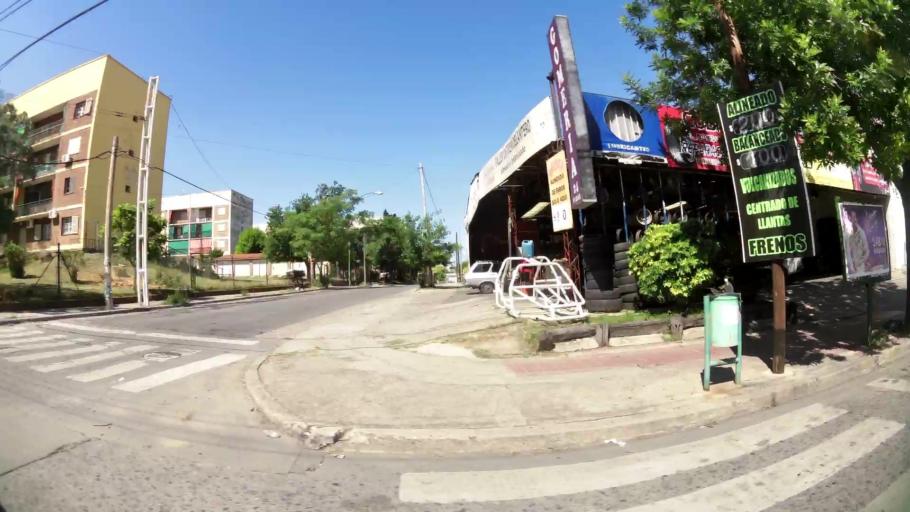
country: AR
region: Cordoba
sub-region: Departamento de Capital
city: Cordoba
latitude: -31.4082
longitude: -64.1582
